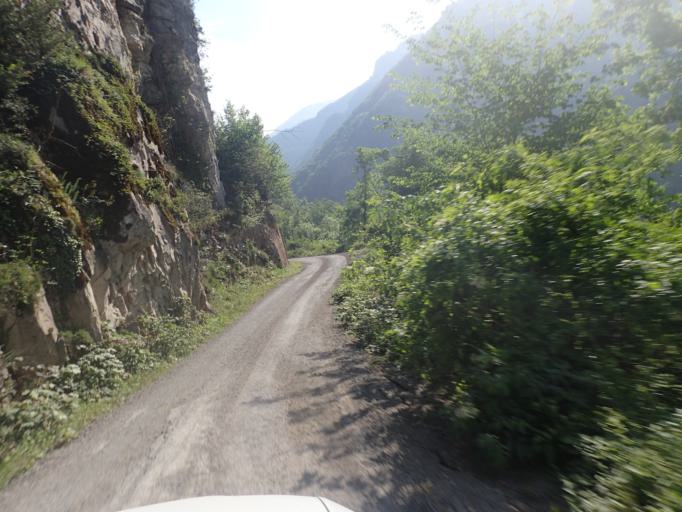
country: TR
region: Ordu
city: Topcam
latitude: 40.7064
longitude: 37.8496
